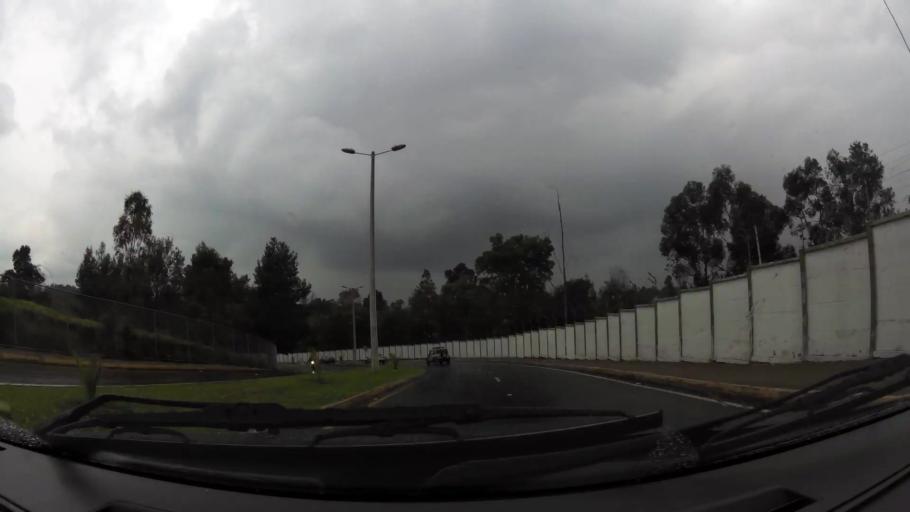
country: EC
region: Pichincha
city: Sangolqui
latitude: -0.3129
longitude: -78.4481
